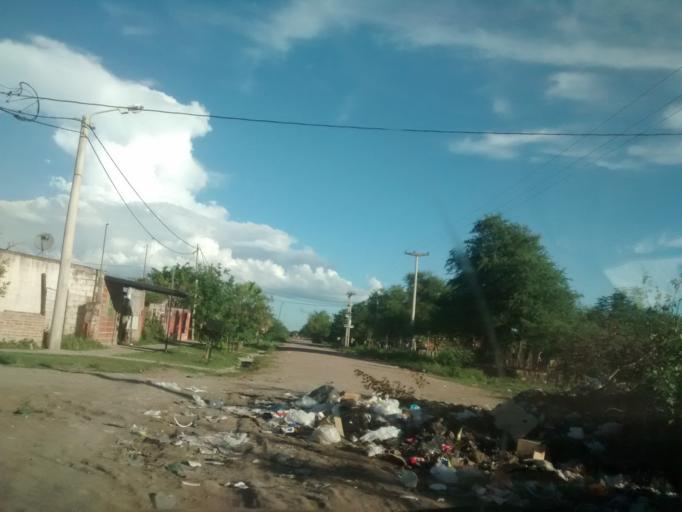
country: AR
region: Chaco
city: Fontana
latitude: -27.4642
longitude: -59.0362
